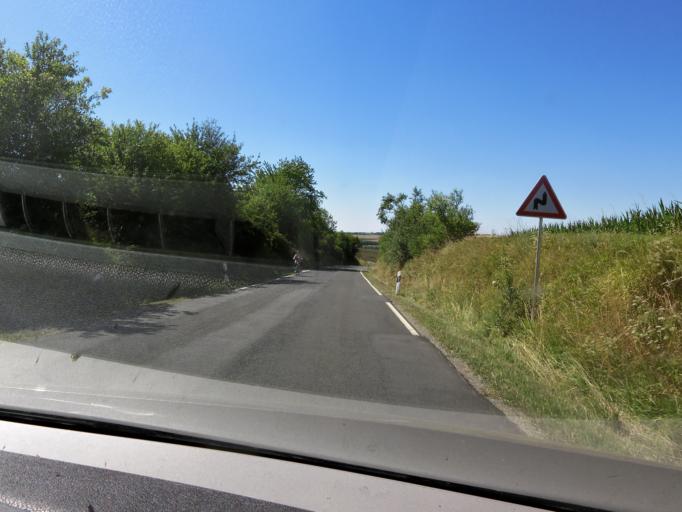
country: DE
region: Bavaria
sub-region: Regierungsbezirk Unterfranken
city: Theilheim
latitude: 49.7509
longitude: 10.0500
